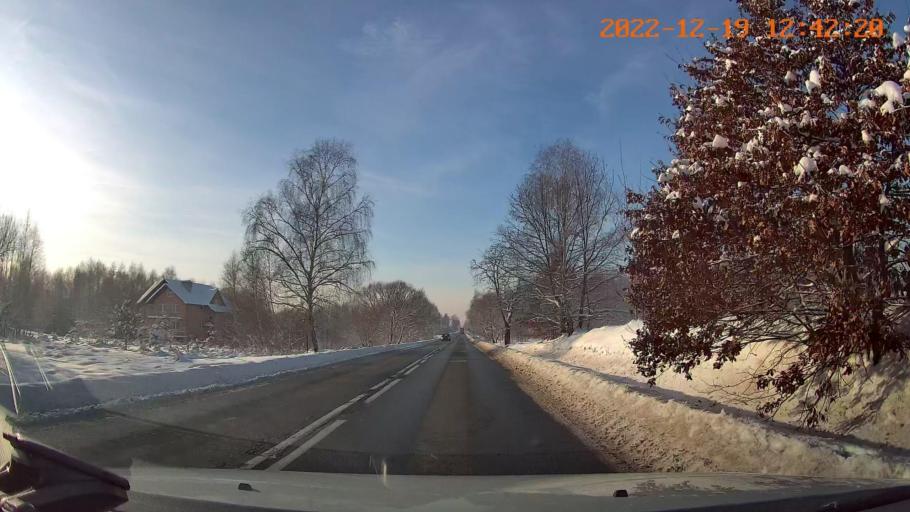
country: PL
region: Lesser Poland Voivodeship
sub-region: Powiat chrzanowski
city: Alwernia
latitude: 50.0606
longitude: 19.5511
